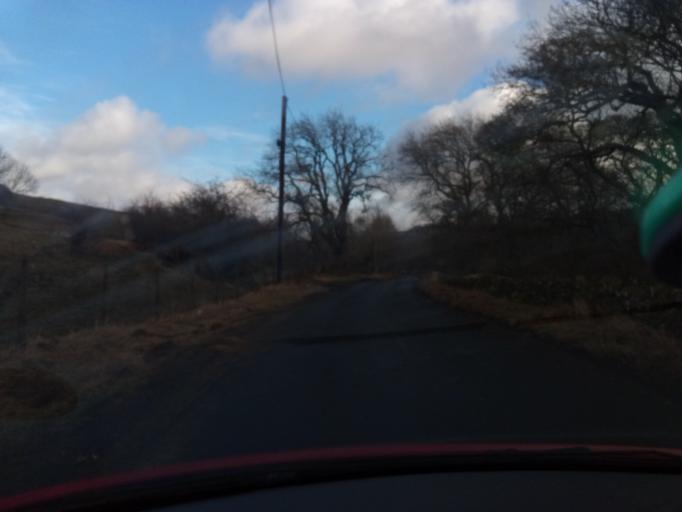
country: GB
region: England
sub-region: Northumberland
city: Otterburn
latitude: 55.2743
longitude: -2.0774
